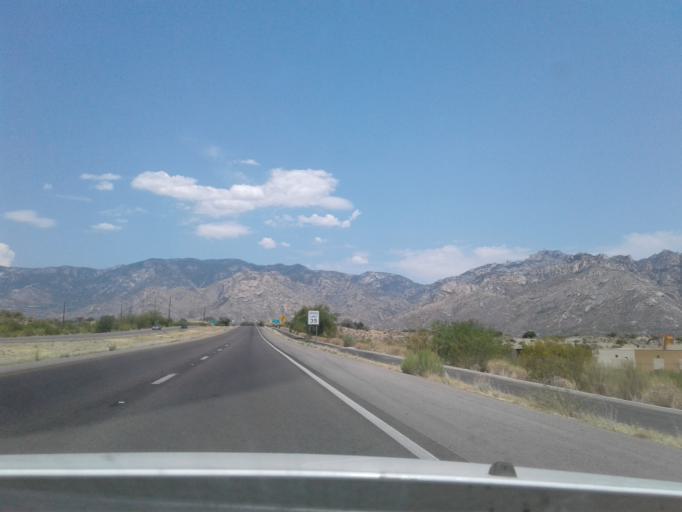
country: US
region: Arizona
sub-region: Pima County
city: Oro Valley
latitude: 32.4270
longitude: -110.9397
